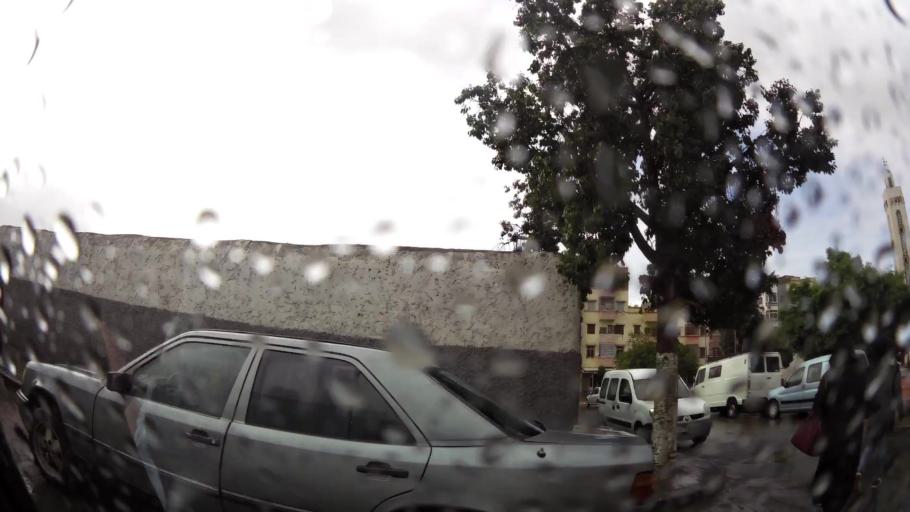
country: MA
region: Grand Casablanca
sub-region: Casablanca
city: Casablanca
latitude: 33.5442
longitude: -7.5719
